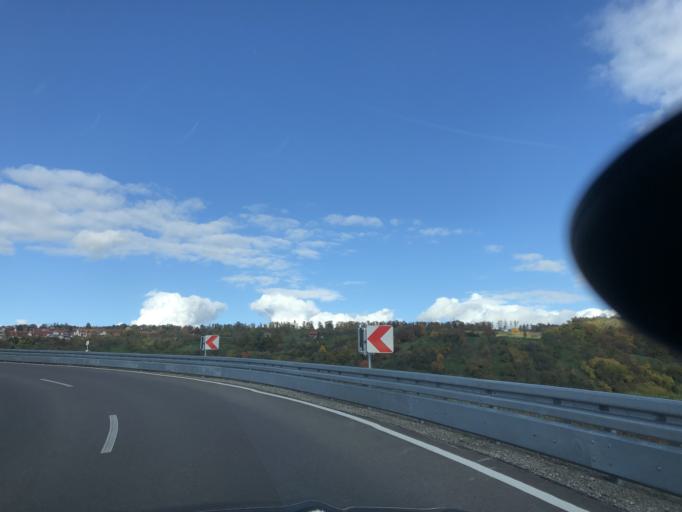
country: DE
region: Baden-Wuerttemberg
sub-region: Regierungsbezirk Stuttgart
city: Allmersbach im Tal
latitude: 48.8815
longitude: 9.4689
